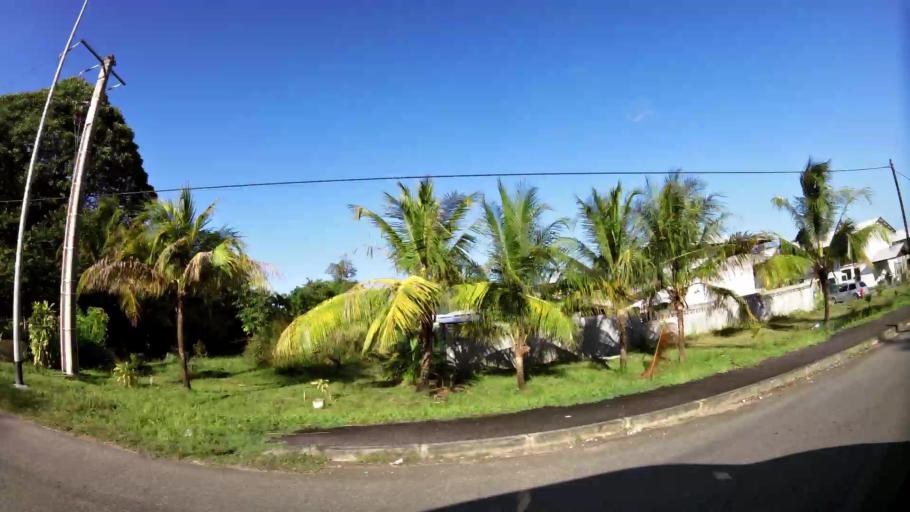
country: GF
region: Guyane
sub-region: Guyane
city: Remire-Montjoly
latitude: 4.8955
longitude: -52.2882
